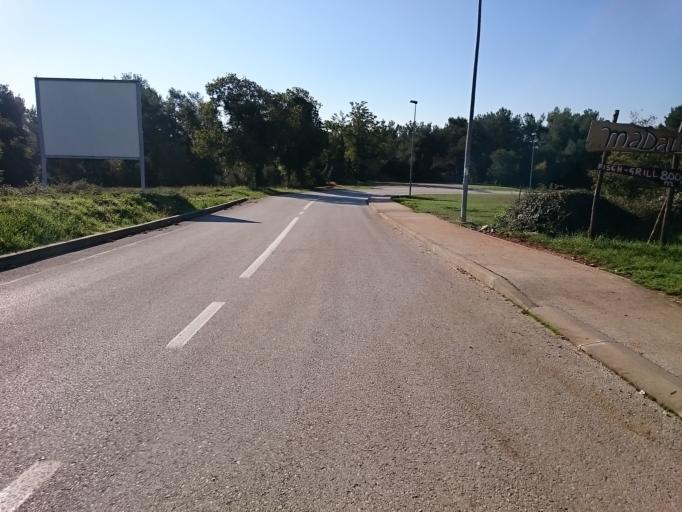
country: HR
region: Istarska
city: Novigrad
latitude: 45.2896
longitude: 13.6098
